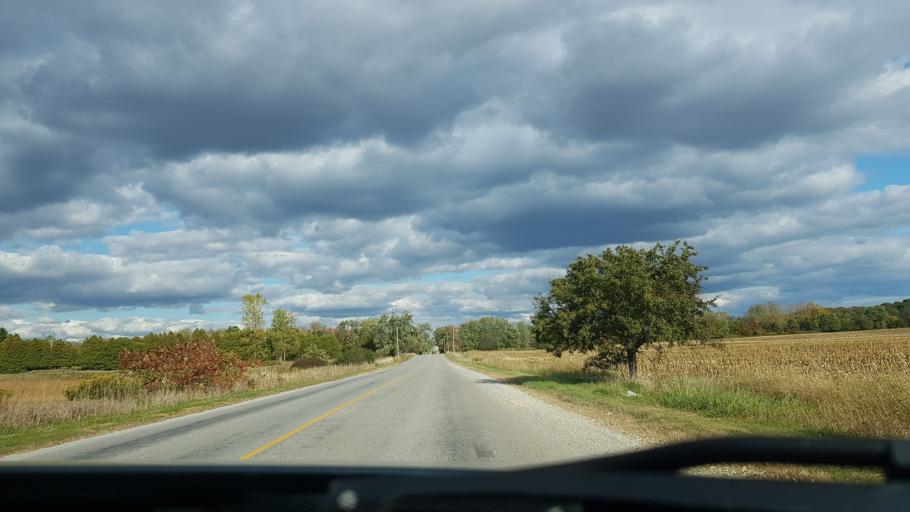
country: CA
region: Ontario
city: Delaware
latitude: 43.0082
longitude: -81.3912
